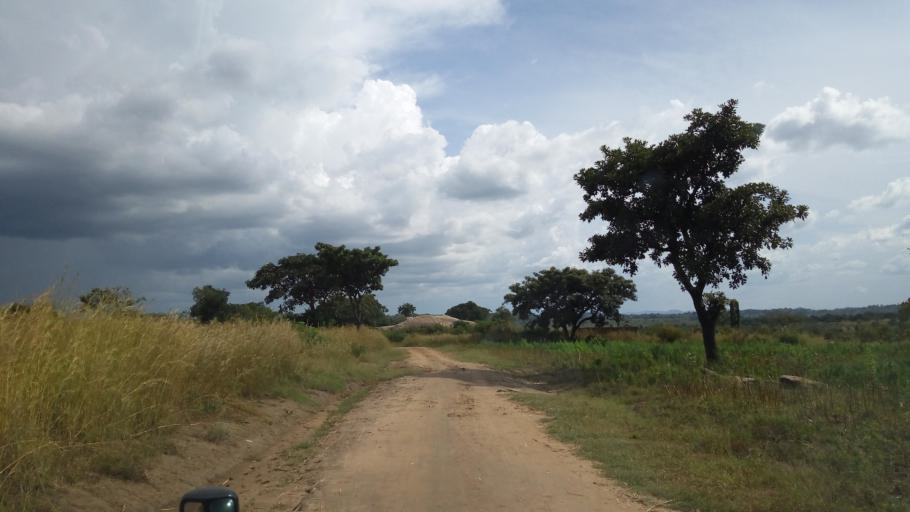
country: UG
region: Northern Region
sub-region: Adjumani District
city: Adjumani
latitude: 3.4354
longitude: 31.8839
